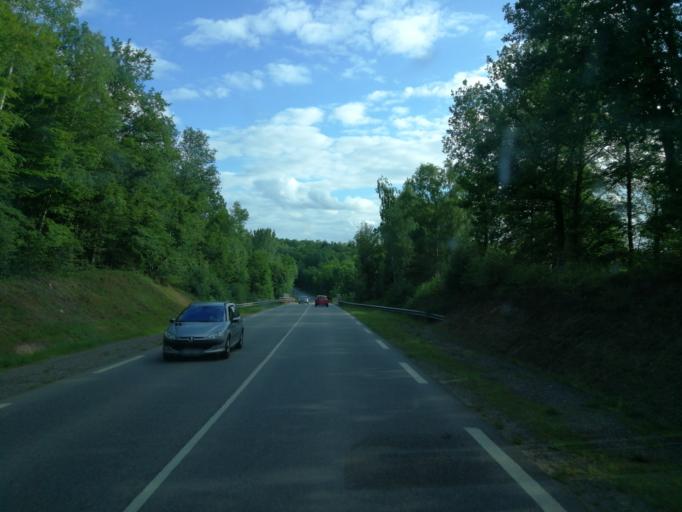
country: FR
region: Haute-Normandie
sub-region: Departement de l'Eure
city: Conches-en-Ouche
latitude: 48.9638
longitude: 0.9286
